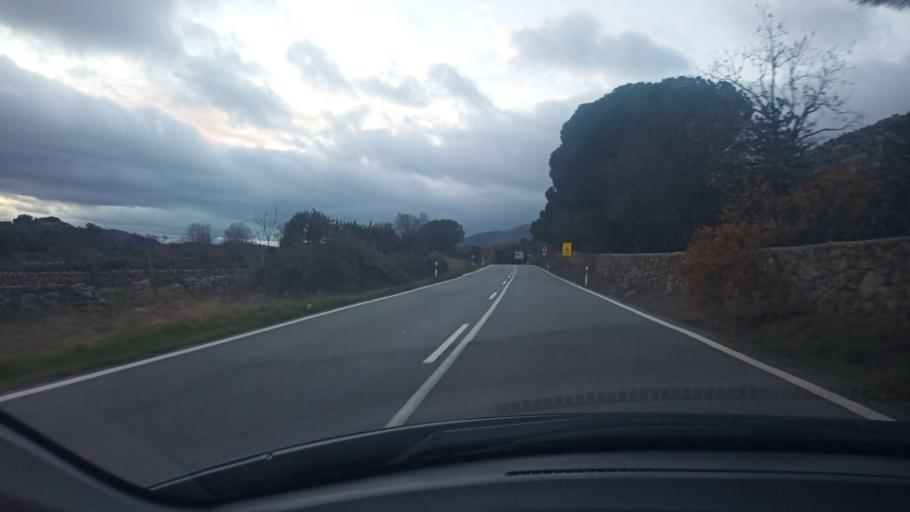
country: ES
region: Madrid
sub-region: Provincia de Madrid
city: Zarzalejo
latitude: 40.5408
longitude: -4.1462
